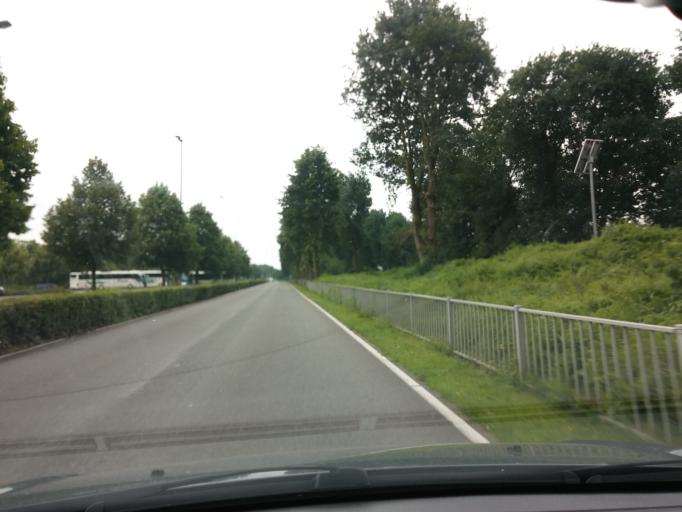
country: DE
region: North Rhine-Westphalia
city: Dorsten
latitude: 51.6228
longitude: 6.9710
